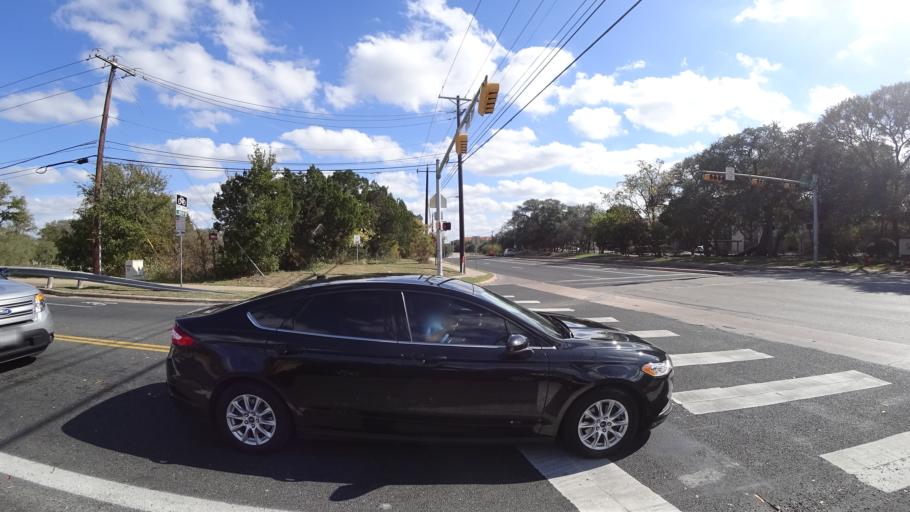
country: US
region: Texas
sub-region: Travis County
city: Wells Branch
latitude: 30.4118
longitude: -97.7220
